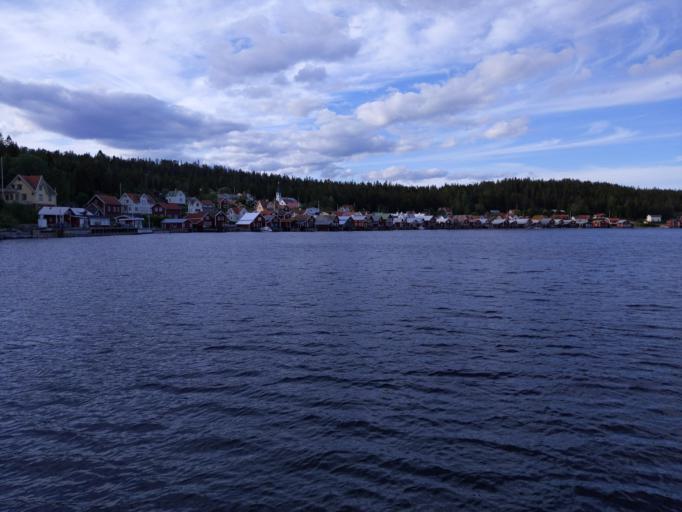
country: SE
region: Vaesternorrland
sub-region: OErnskoeldsviks Kommun
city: Kopmanholmen
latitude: 63.0188
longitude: 18.6470
